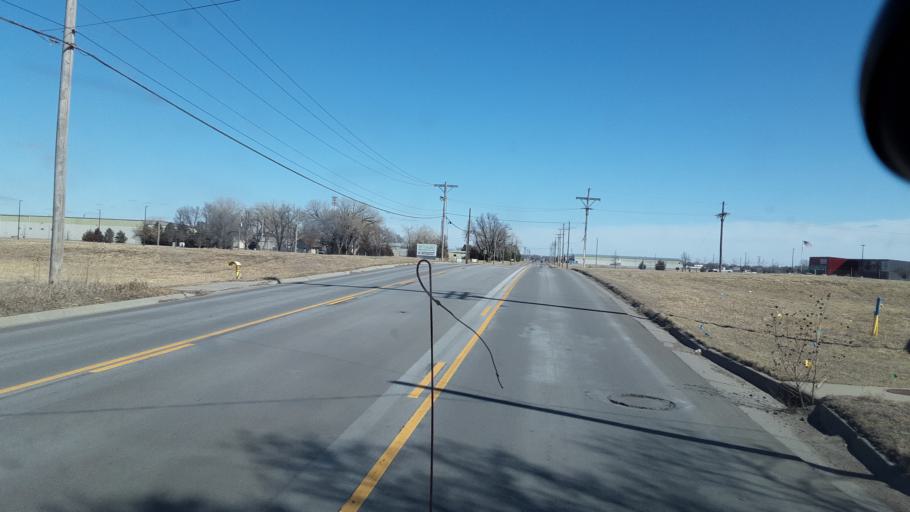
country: US
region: Kansas
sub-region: Reno County
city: Hutchinson
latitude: 38.0576
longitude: -97.8764
